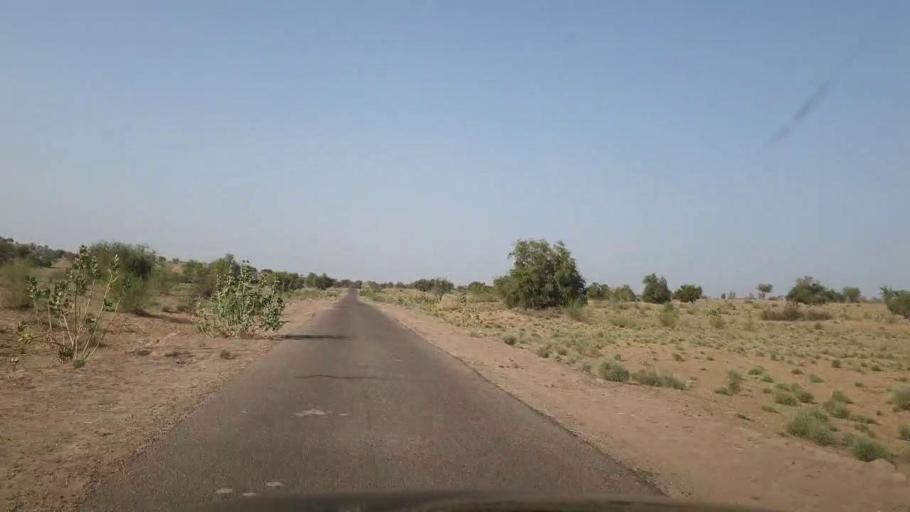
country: PK
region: Sindh
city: Islamkot
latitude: 25.1423
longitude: 70.5187
